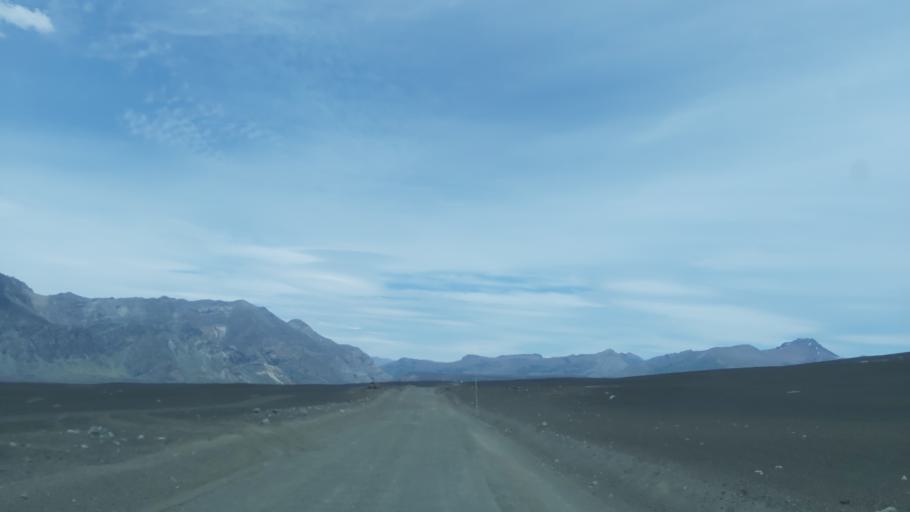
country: AR
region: Neuquen
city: Andacollo
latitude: -37.4266
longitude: -71.2871
